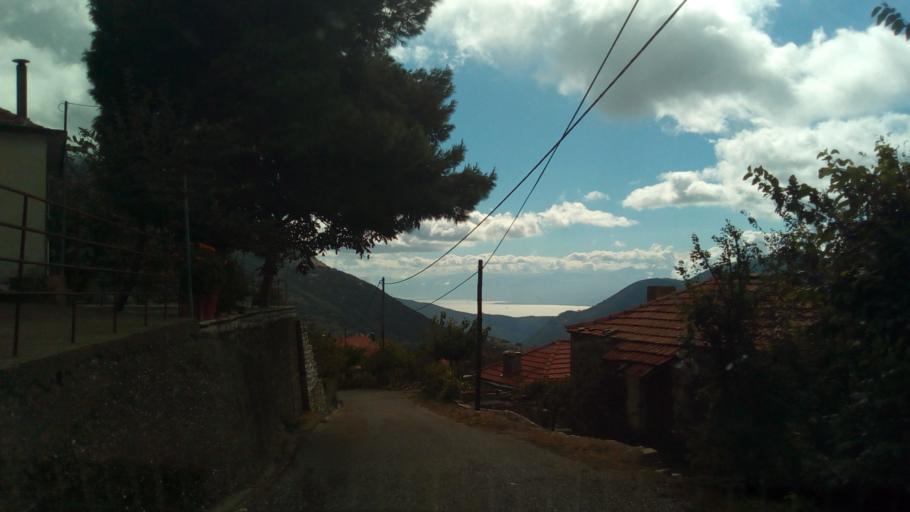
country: GR
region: West Greece
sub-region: Nomos Aitolias kai Akarnanias
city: Nafpaktos
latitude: 38.4981
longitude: 21.8424
